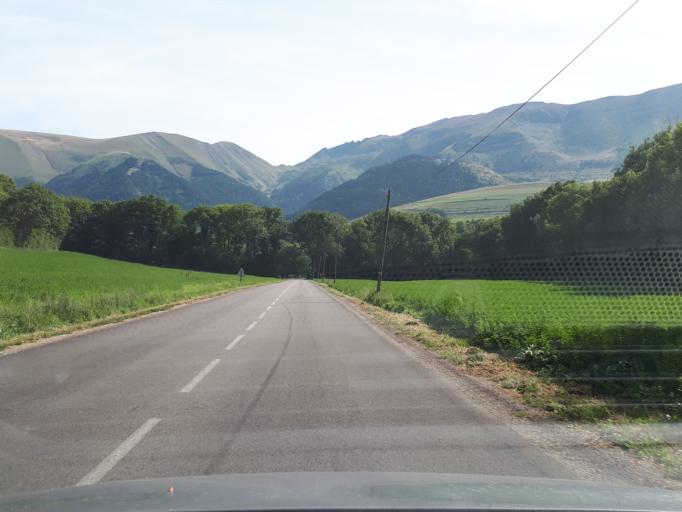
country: FR
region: Rhone-Alpes
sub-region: Departement de l'Isere
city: Pierre-Chatel
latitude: 44.9632
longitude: 5.7844
